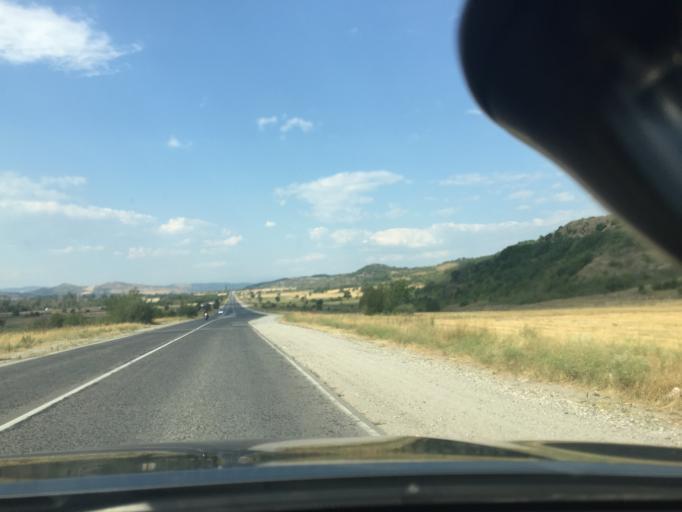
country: BG
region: Kyustendil
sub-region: Obshtina Boboshevo
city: Boboshevo
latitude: 42.1635
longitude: 23.0434
